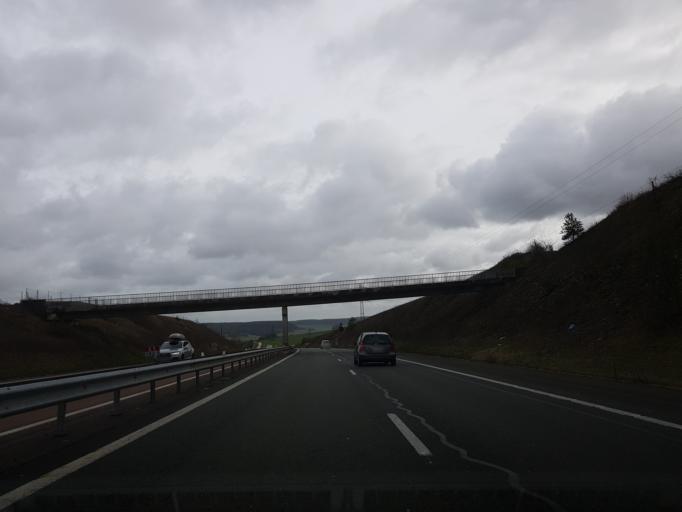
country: FR
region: Champagne-Ardenne
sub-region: Departement de la Haute-Marne
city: Chateauvillain
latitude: 48.0820
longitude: 4.8635
